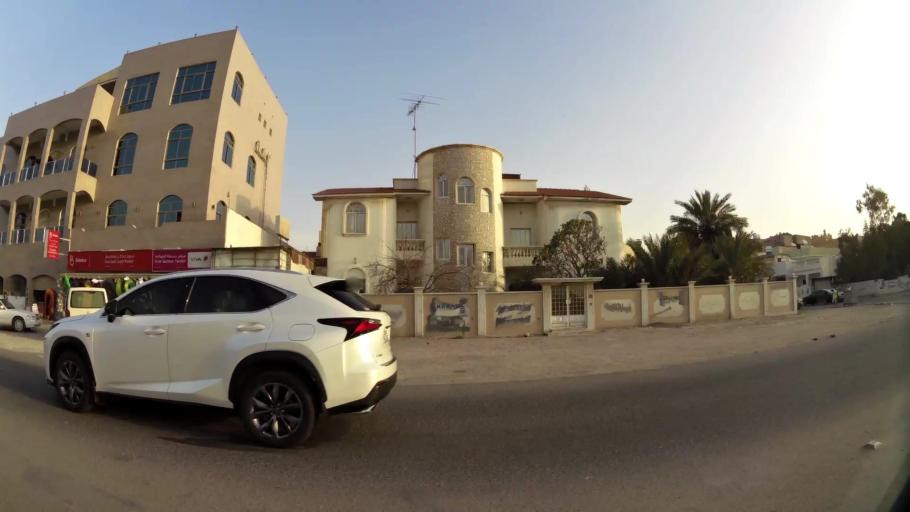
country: BH
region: Manama
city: Jidd Hafs
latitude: 26.1963
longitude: 50.4840
